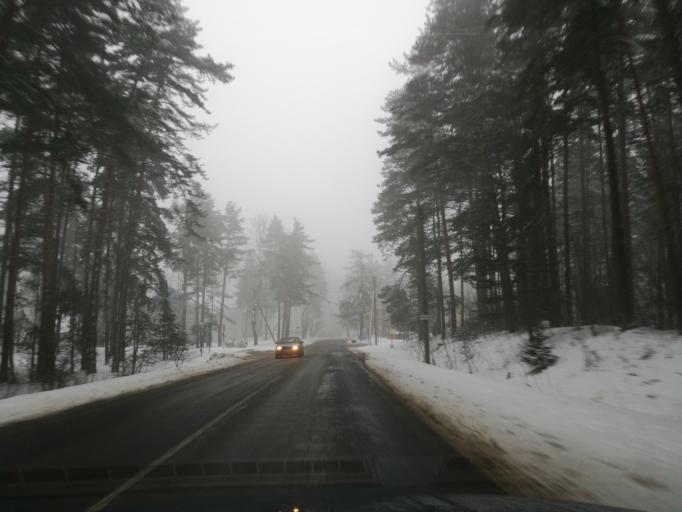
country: LT
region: Utenos apskritis
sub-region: Anyksciai
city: Anyksciai
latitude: 55.5100
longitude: 25.0959
